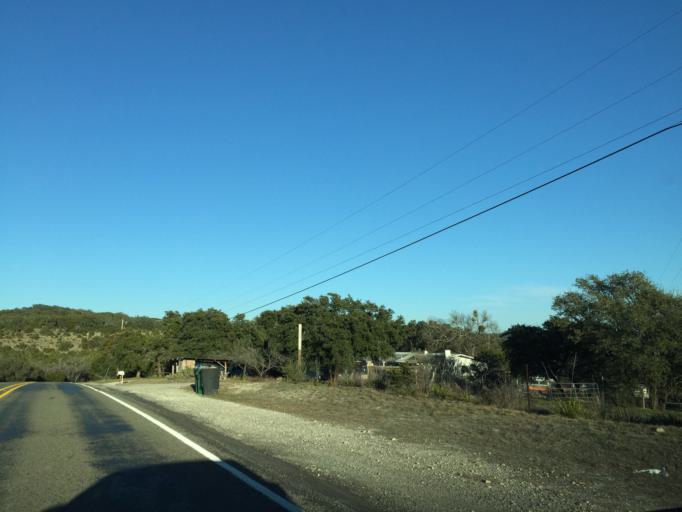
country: US
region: Texas
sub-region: Travis County
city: Lago Vista
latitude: 30.5217
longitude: -98.0581
